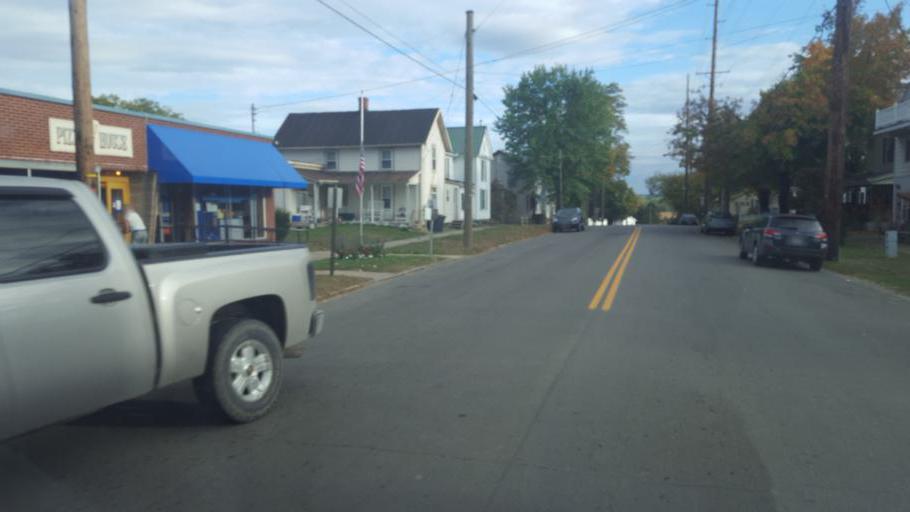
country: US
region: Ohio
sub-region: Ashland County
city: Ashland
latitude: 40.8032
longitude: -82.1952
